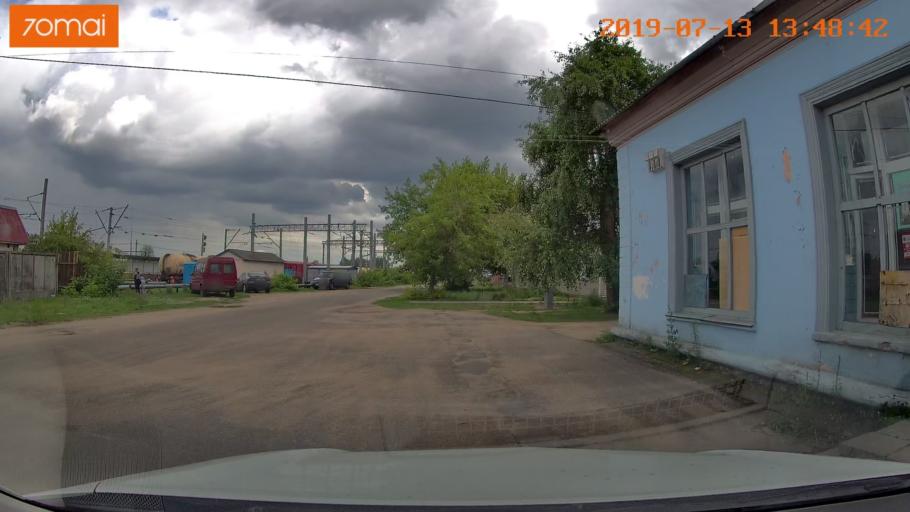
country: BY
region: Mogilev
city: Asipovichy
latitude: 53.2986
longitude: 28.6440
